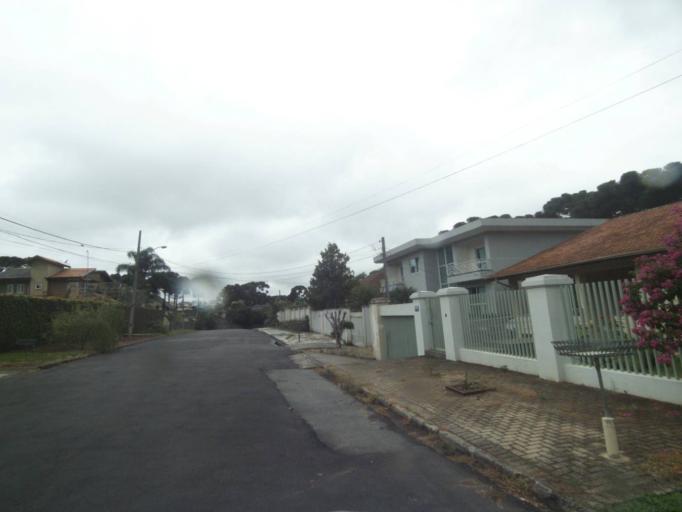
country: BR
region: Parana
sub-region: Curitiba
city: Curitiba
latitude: -25.4227
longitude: -49.3304
